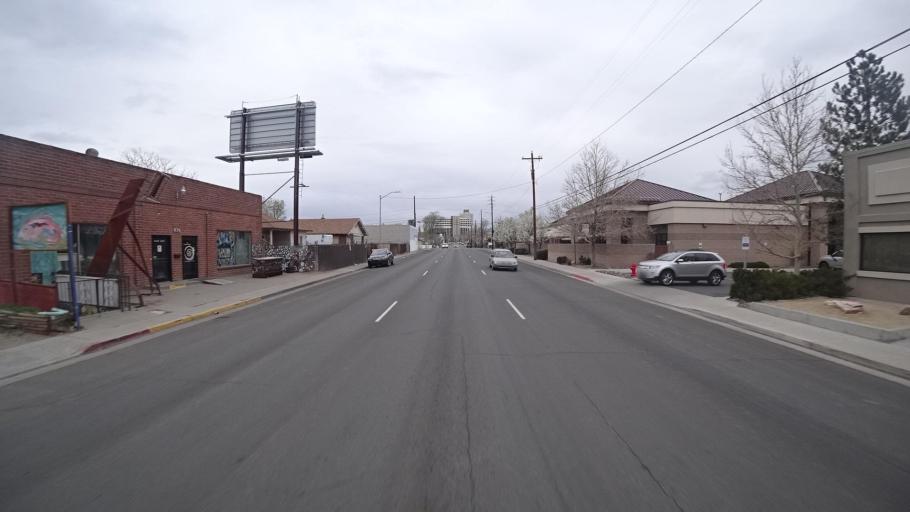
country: US
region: Nevada
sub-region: Washoe County
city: Reno
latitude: 39.5274
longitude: -119.7995
